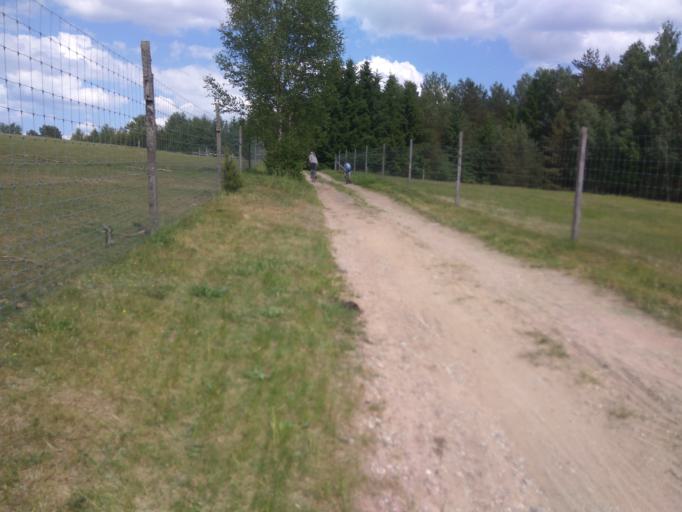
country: LV
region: Kuldigas Rajons
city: Kuldiga
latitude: 56.8870
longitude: 21.9289
